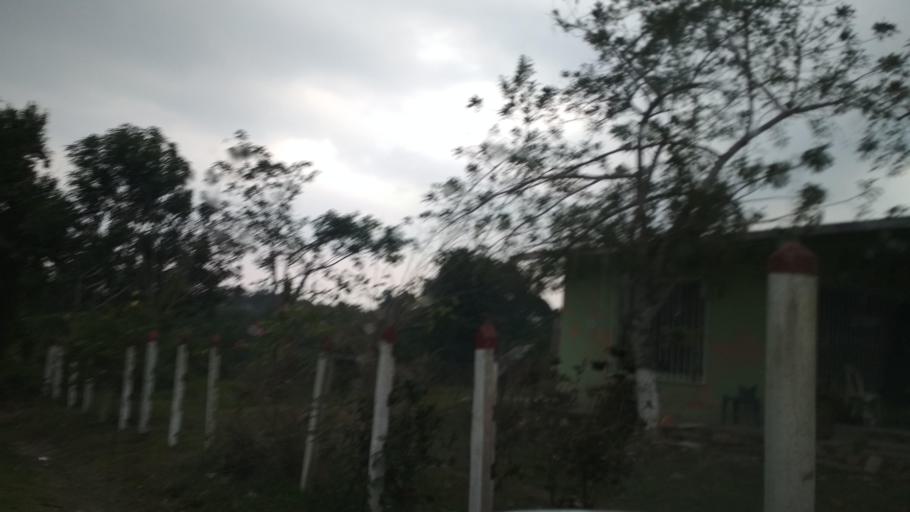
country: MM
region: Shan
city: Taunggyi
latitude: 20.3327
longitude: 97.3107
